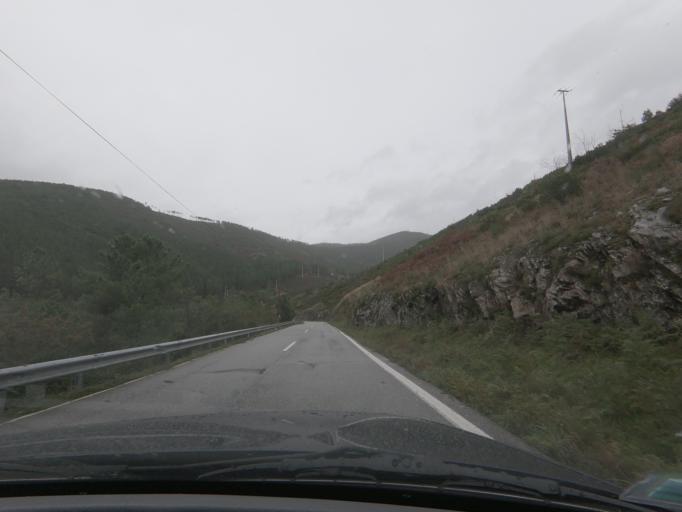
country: PT
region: Vila Real
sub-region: Mondim de Basto
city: Mondim de Basto
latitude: 41.3630
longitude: -7.9203
